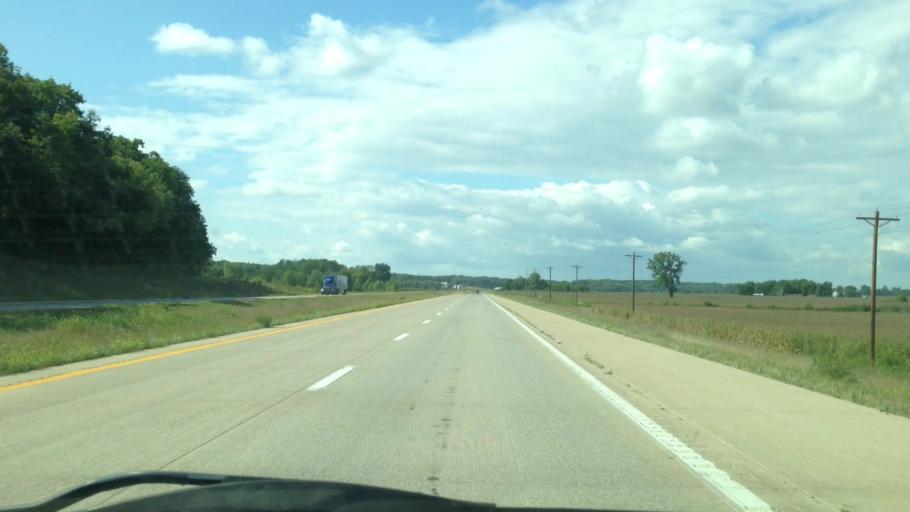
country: US
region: Illinois
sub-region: Hancock County
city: Warsaw
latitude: 40.3181
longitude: -91.5774
